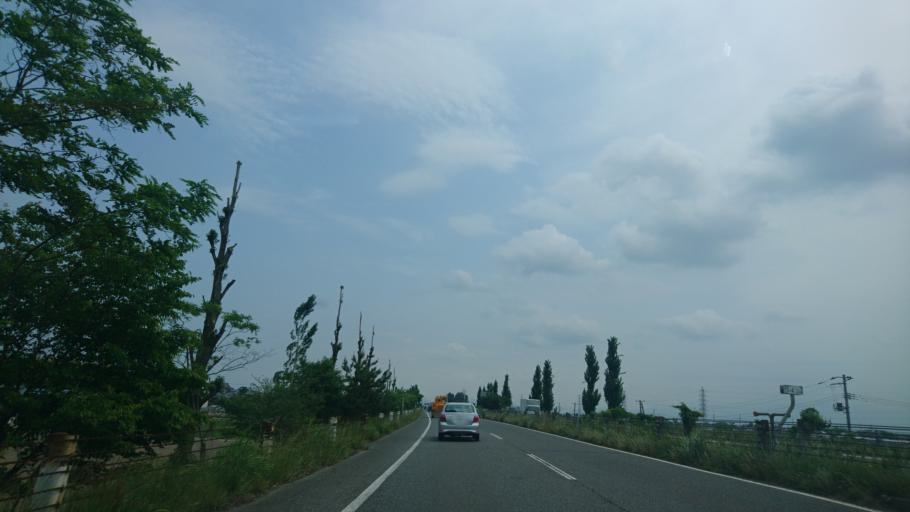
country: JP
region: Niigata
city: Kameda-honcho
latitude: 37.9360
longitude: 139.1682
